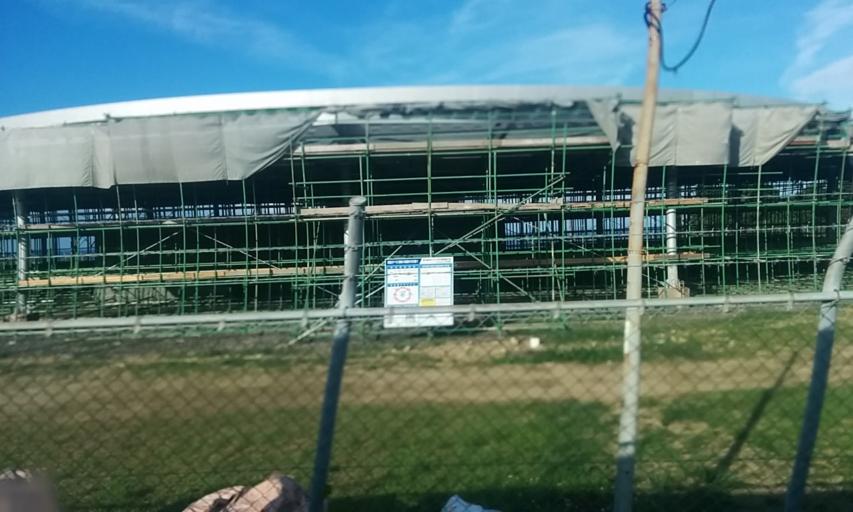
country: JP
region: Kagoshima
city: Nishinoomote
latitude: 30.3790
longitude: 130.6624
